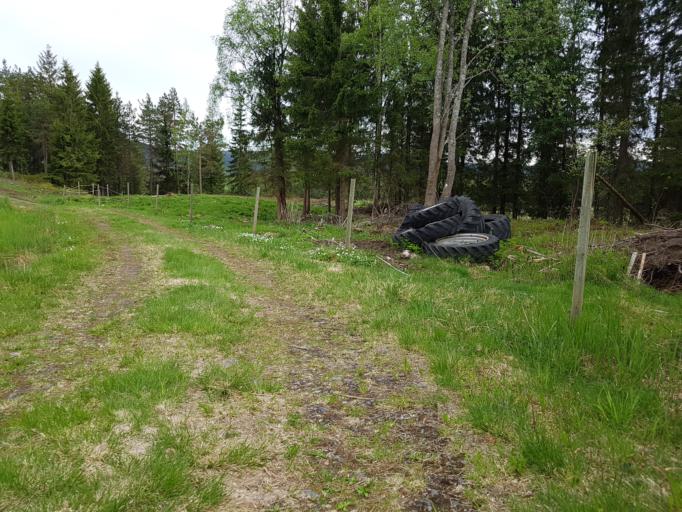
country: NO
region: Nord-Trondelag
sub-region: Levanger
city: Skogn
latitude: 63.6317
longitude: 11.2542
